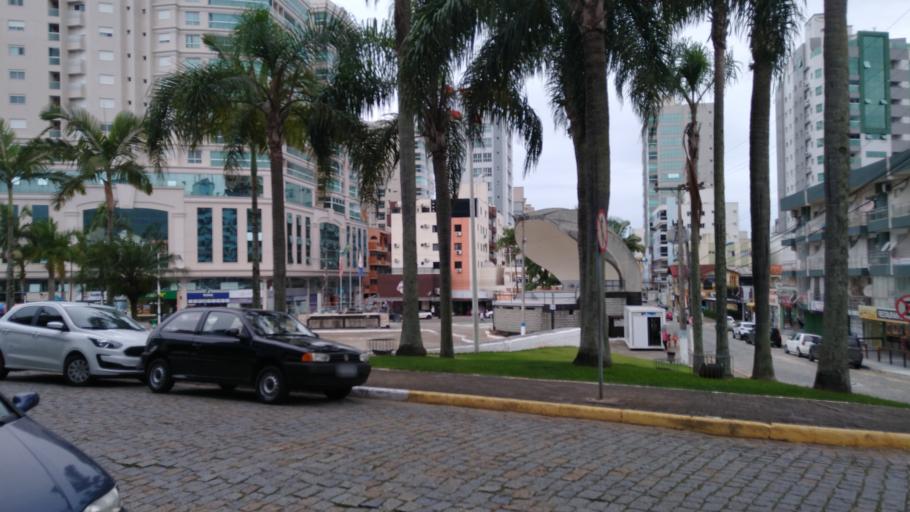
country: BR
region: Santa Catarina
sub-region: Itapema
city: Itapema
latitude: -27.0977
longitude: -48.6170
